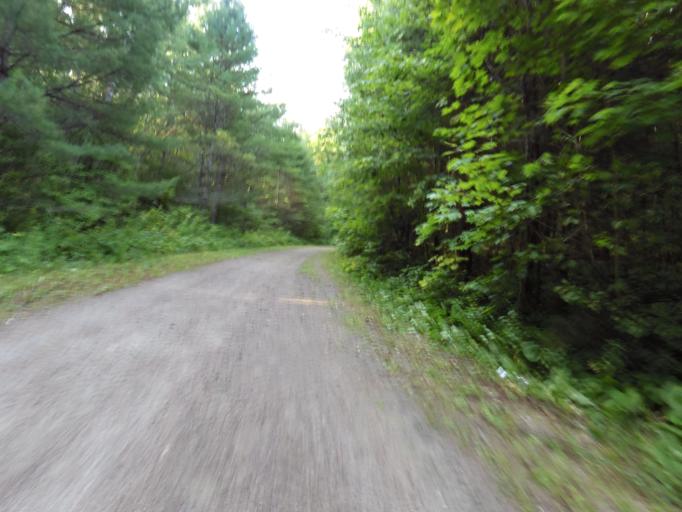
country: CA
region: Quebec
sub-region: Outaouais
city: Maniwaki
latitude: 46.2671
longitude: -76.0186
